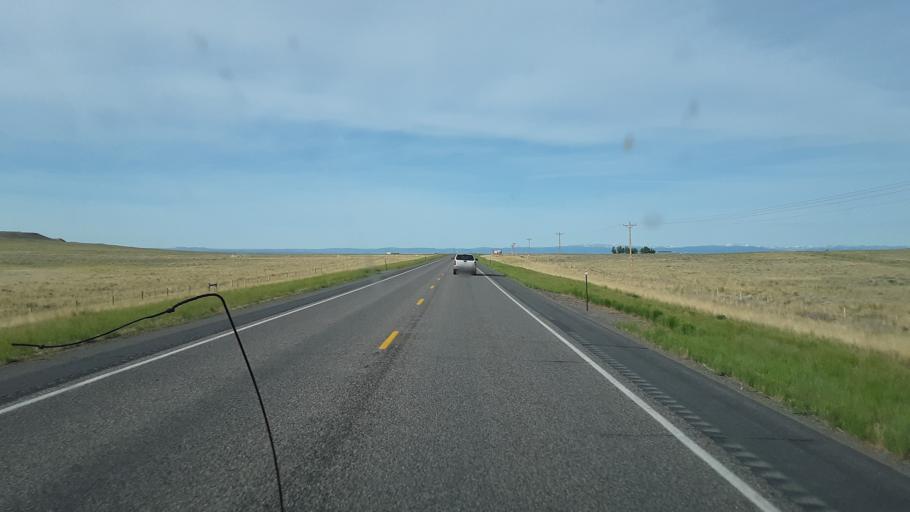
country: US
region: Wyoming
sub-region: Fremont County
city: Riverton
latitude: 43.1578
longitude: -108.2721
